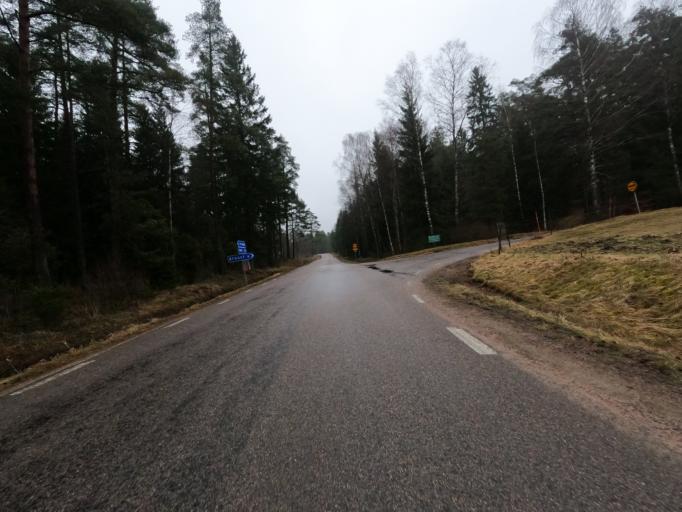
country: SE
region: Halland
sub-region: Hylte Kommun
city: Torup
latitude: 56.7969
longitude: 13.1972
